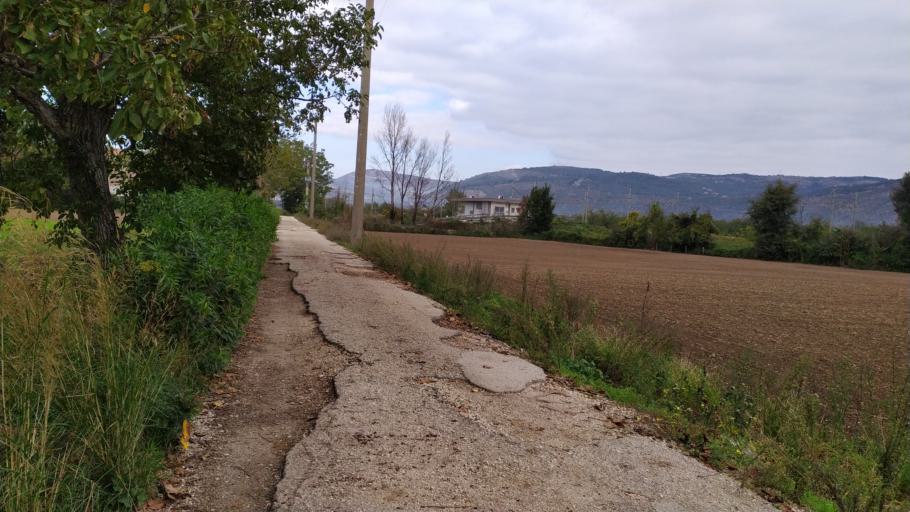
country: IT
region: Campania
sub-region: Provincia di Caserta
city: Montedecoro
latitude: 41.0168
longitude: 14.4058
